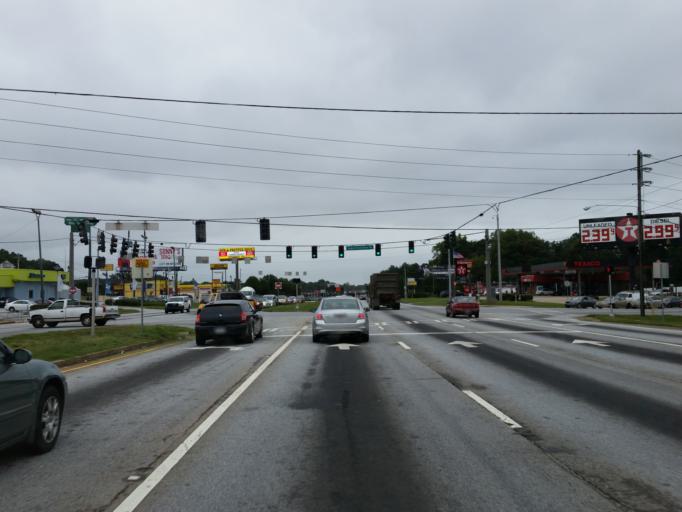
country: US
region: Georgia
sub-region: Clayton County
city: Riverdale
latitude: 33.5835
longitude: -84.3784
